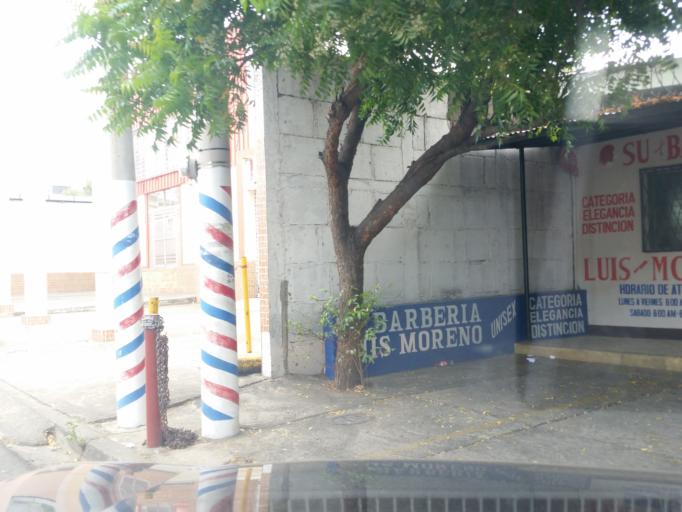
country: NI
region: Managua
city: Managua
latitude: 12.1183
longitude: -86.2551
